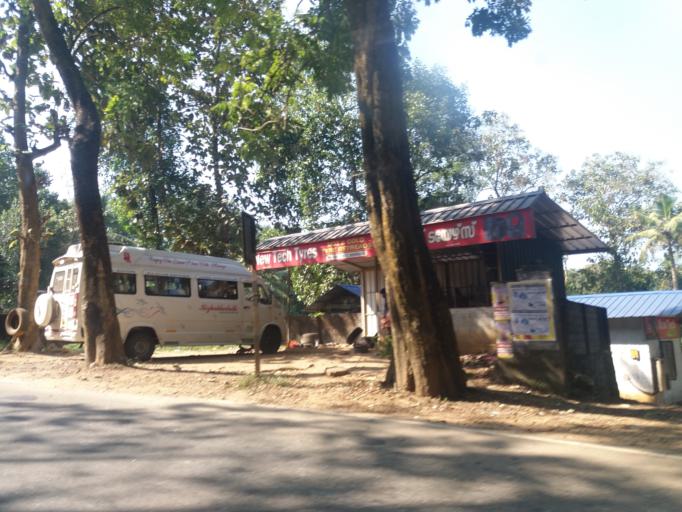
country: IN
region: Kerala
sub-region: Ernakulam
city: Muvattupuzha
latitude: 9.8882
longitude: 76.6994
